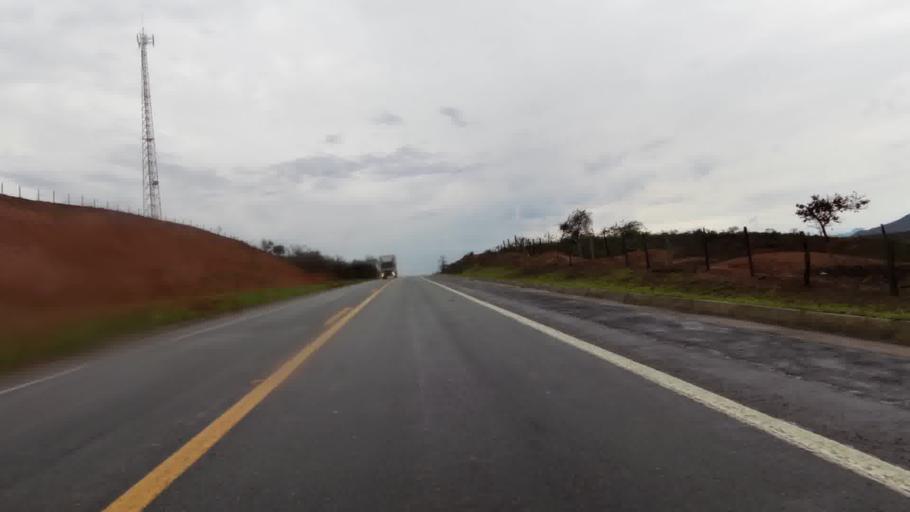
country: BR
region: Rio de Janeiro
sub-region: Campos Dos Goytacazes
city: Campos
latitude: -21.4851
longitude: -41.3401
